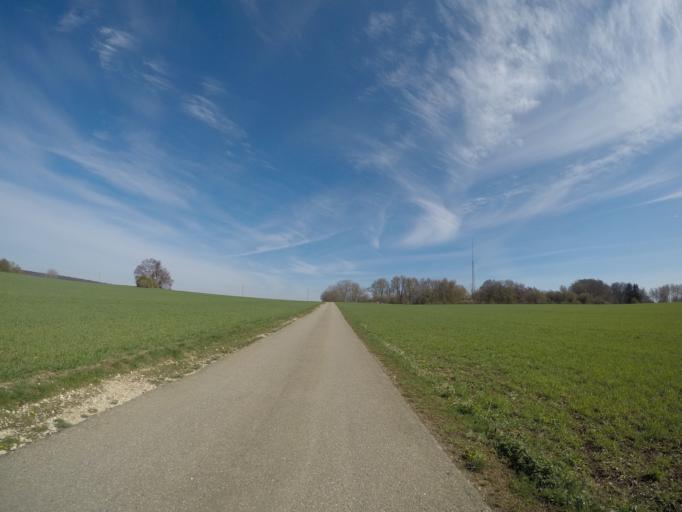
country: DE
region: Baden-Wuerttemberg
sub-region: Tuebingen Region
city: Laichingen
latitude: 48.4796
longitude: 9.6938
